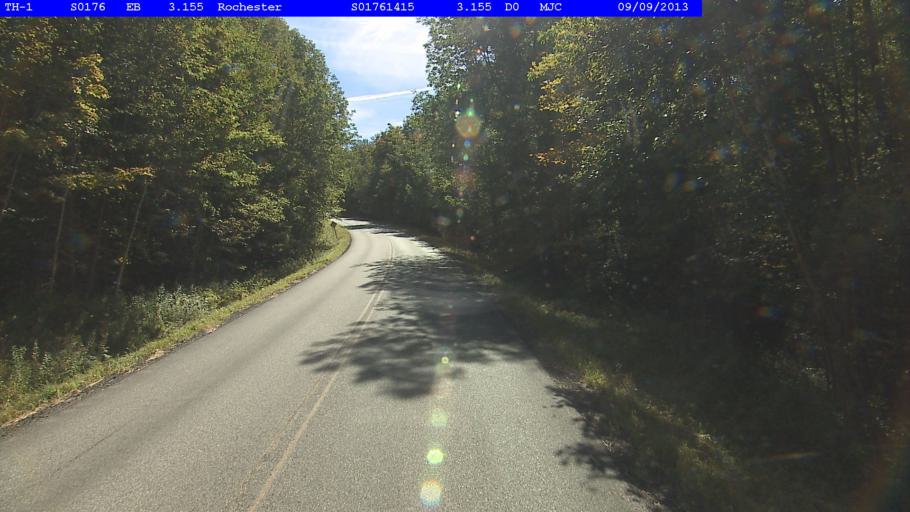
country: US
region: Vermont
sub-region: Orange County
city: Randolph
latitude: 43.8594
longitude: -72.7614
